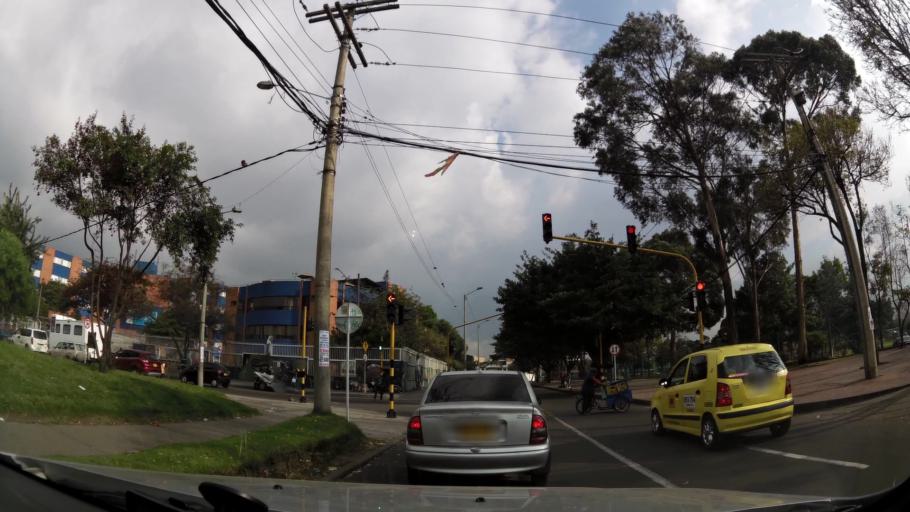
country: CO
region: Bogota D.C.
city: Bogota
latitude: 4.5719
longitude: -74.1292
